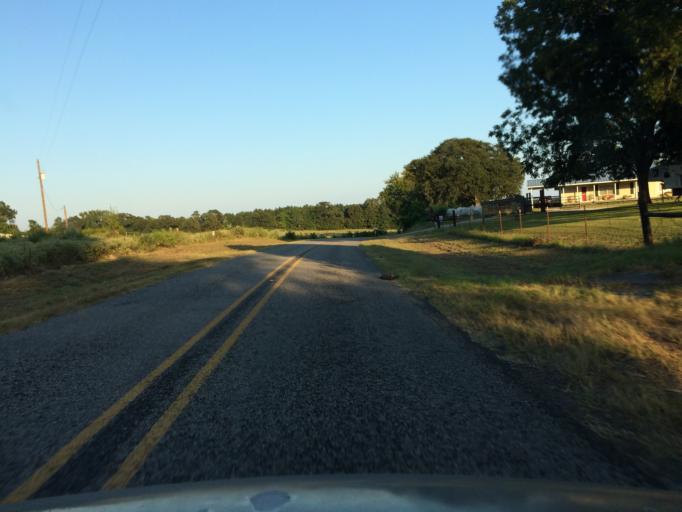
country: US
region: Texas
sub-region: Wood County
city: Hawkins
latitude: 32.7418
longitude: -95.2668
